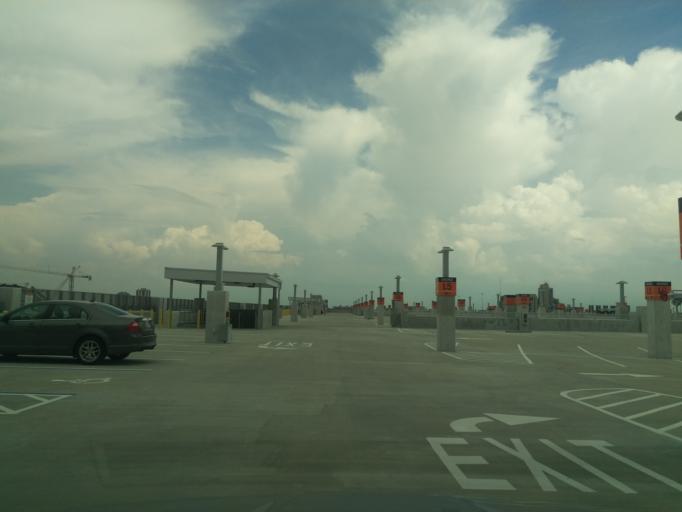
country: US
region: Florida
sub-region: Osceola County
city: Celebration
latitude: 28.3694
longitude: -81.5215
